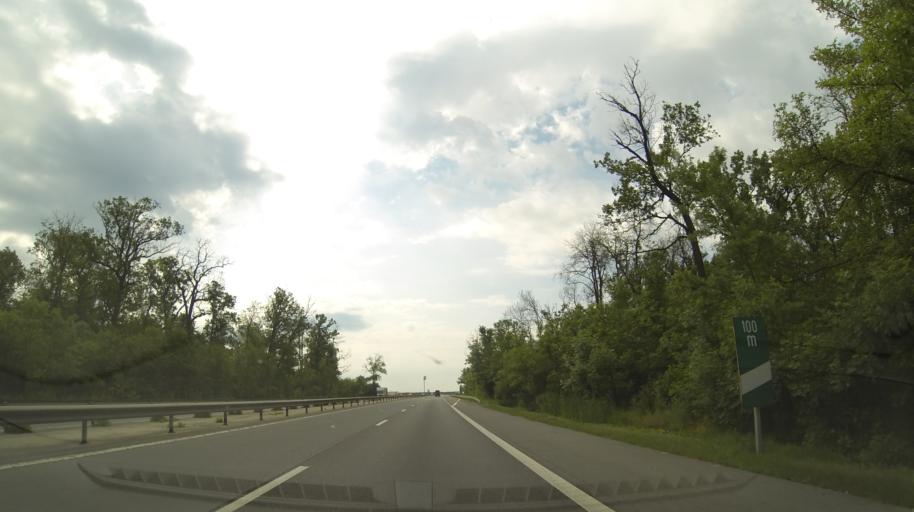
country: RO
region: Dambovita
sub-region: Comuna Corbii Mari
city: Grozavesti
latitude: 44.6109
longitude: 25.4505
